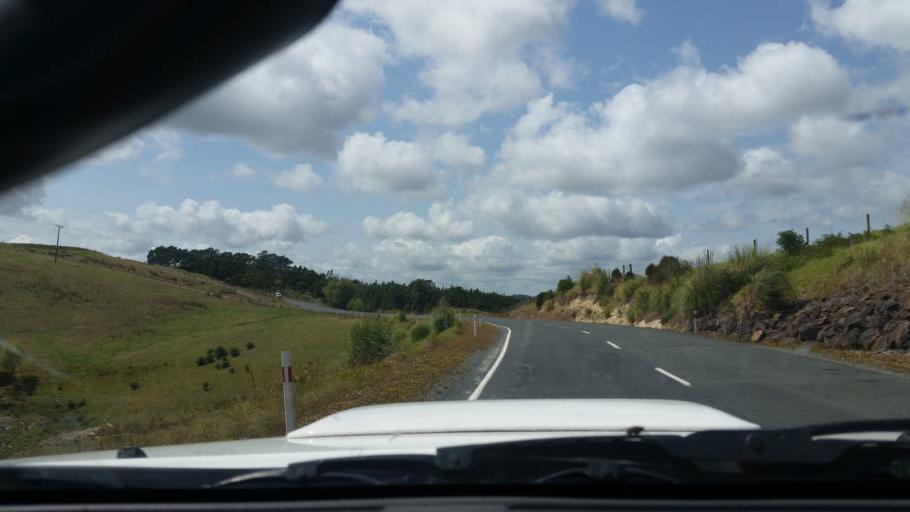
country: NZ
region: Auckland
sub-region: Auckland
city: Wellsford
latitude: -36.1376
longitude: 174.4811
